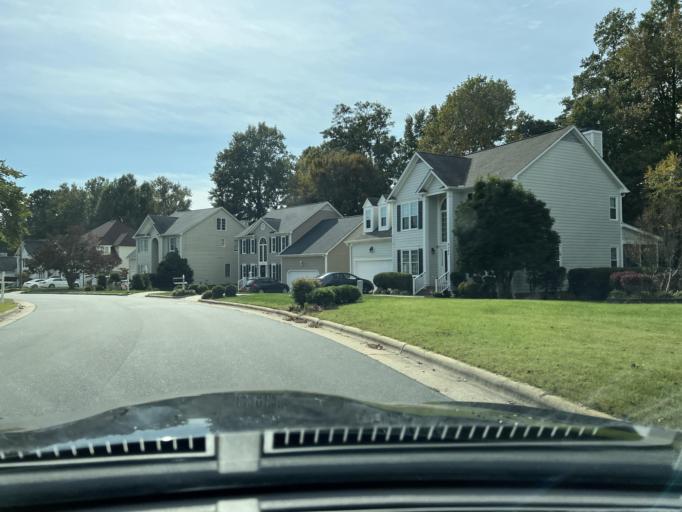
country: US
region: North Carolina
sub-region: Wake County
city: Wake Forest
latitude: 35.9011
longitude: -78.5828
